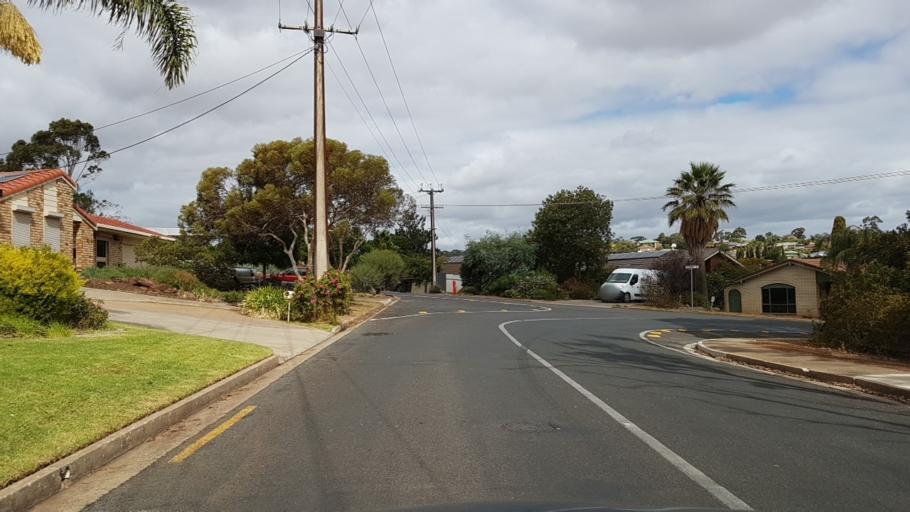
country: AU
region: South Australia
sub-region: Gawler
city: Gawler
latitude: -34.6088
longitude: 138.7542
